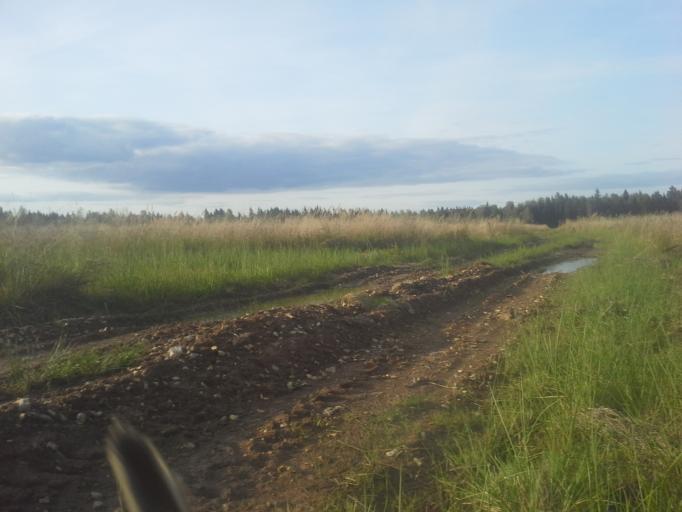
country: RU
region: Moskovskaya
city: Kievskij
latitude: 55.3541
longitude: 36.9583
